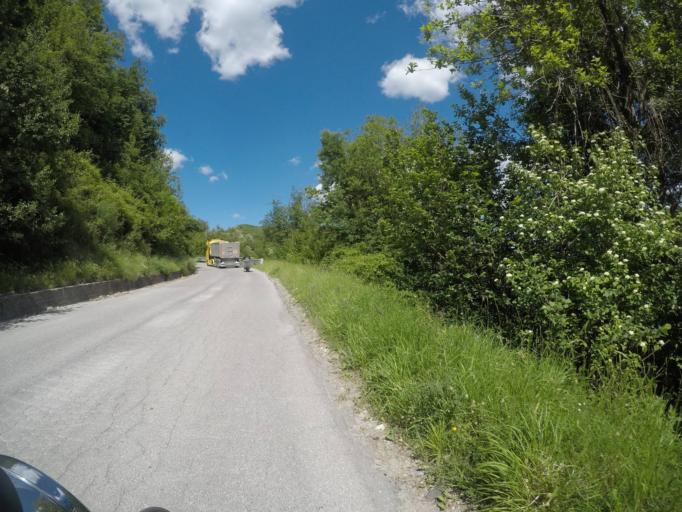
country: IT
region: Tuscany
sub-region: Provincia di Lucca
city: Minucciano
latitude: 44.1635
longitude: 10.2117
